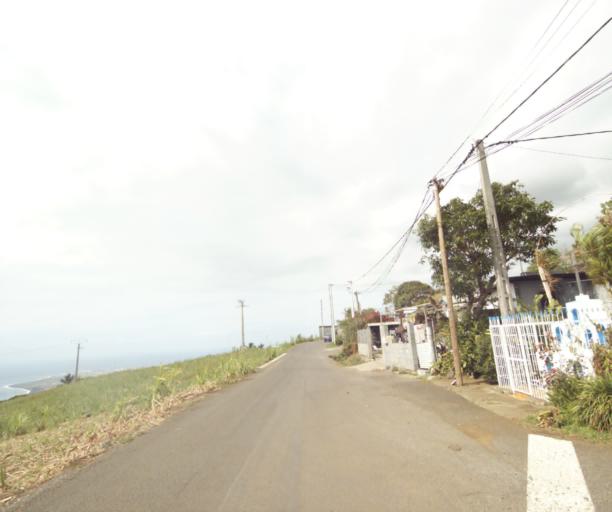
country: RE
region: Reunion
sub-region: Reunion
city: Saint-Paul
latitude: -21.0339
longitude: 55.2902
